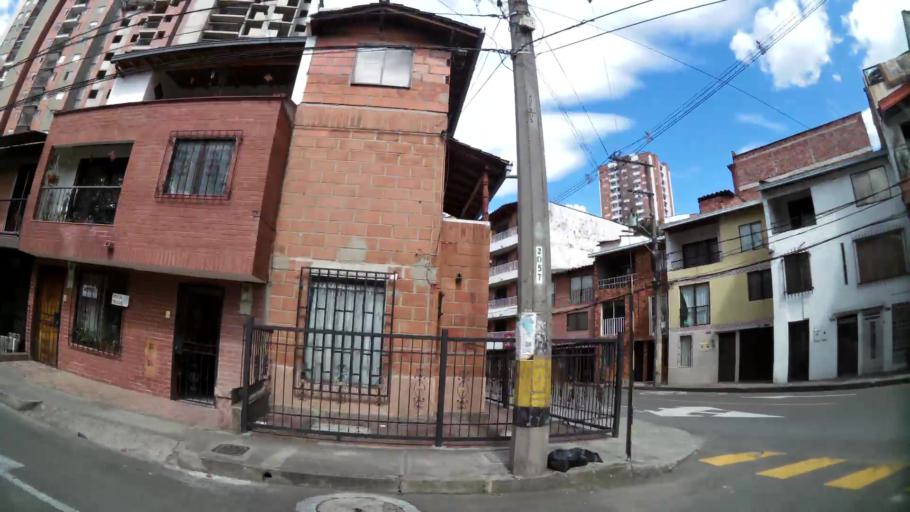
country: CO
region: Antioquia
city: Sabaneta
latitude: 6.1542
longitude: -75.6114
